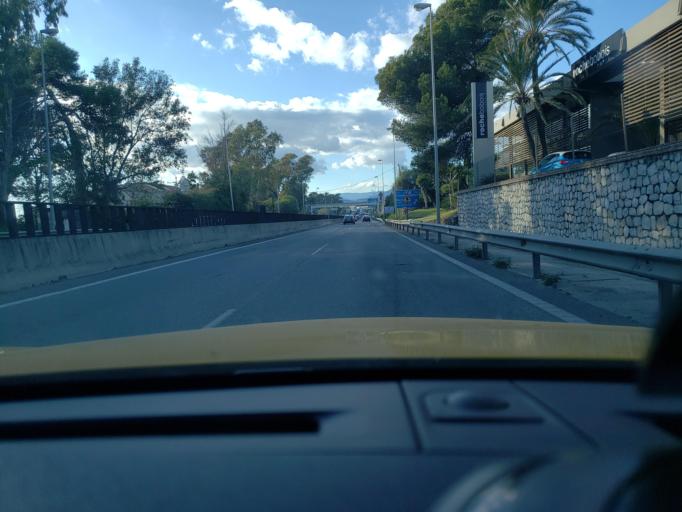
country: ES
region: Andalusia
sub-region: Provincia de Malaga
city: Marbella
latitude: 36.5058
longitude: -4.8471
